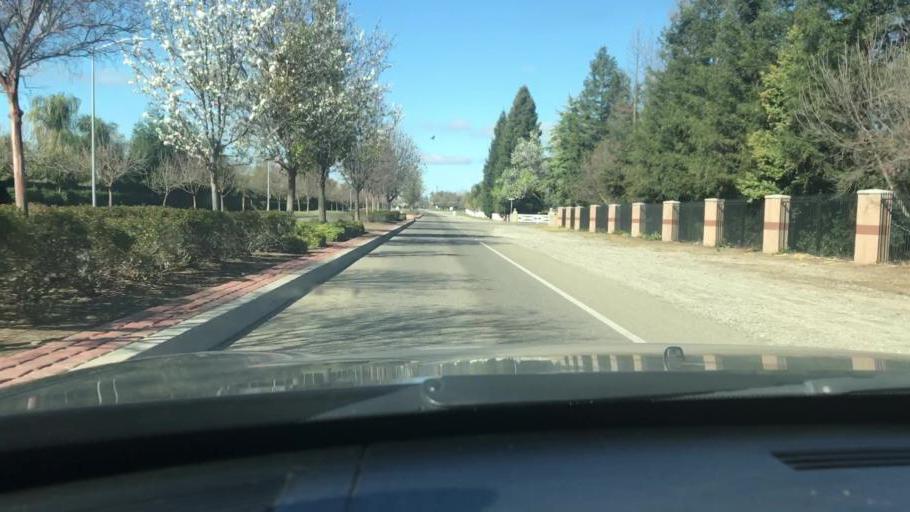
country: US
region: California
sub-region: Fresno County
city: Clovis
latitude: 36.8665
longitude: -119.6784
